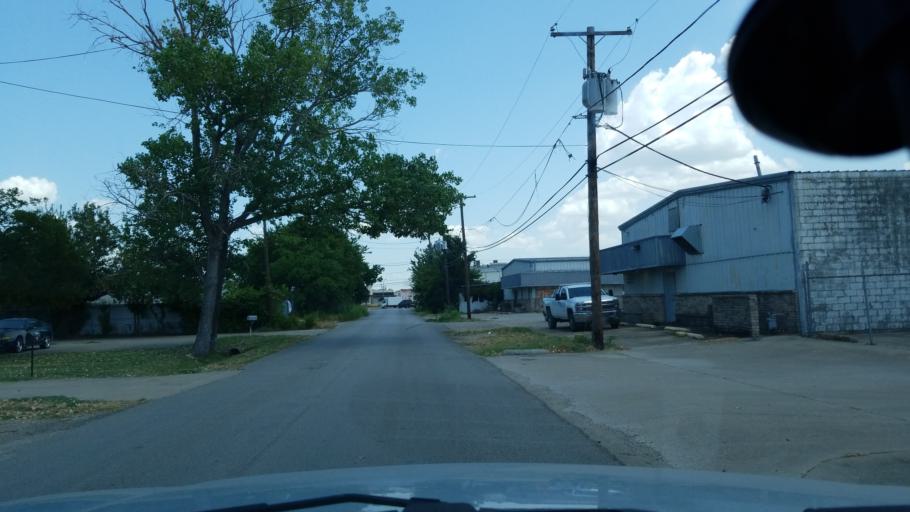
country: US
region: Texas
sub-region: Dallas County
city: Farmers Branch
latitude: 32.8913
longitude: -96.8922
